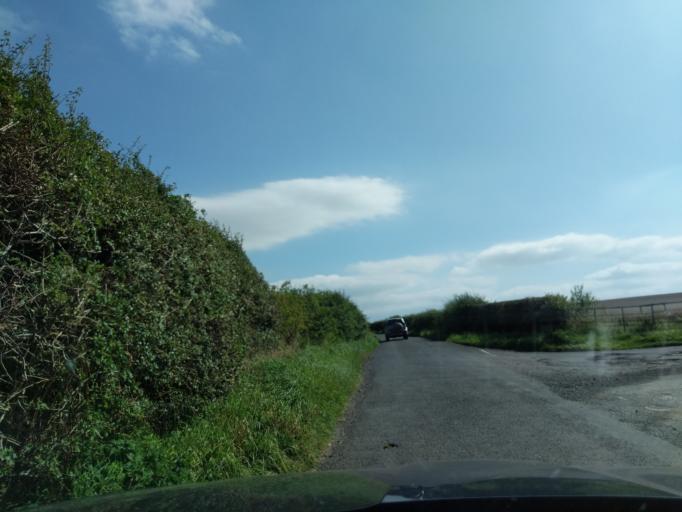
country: GB
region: England
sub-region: Northumberland
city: Ford
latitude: 55.6675
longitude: -2.1650
